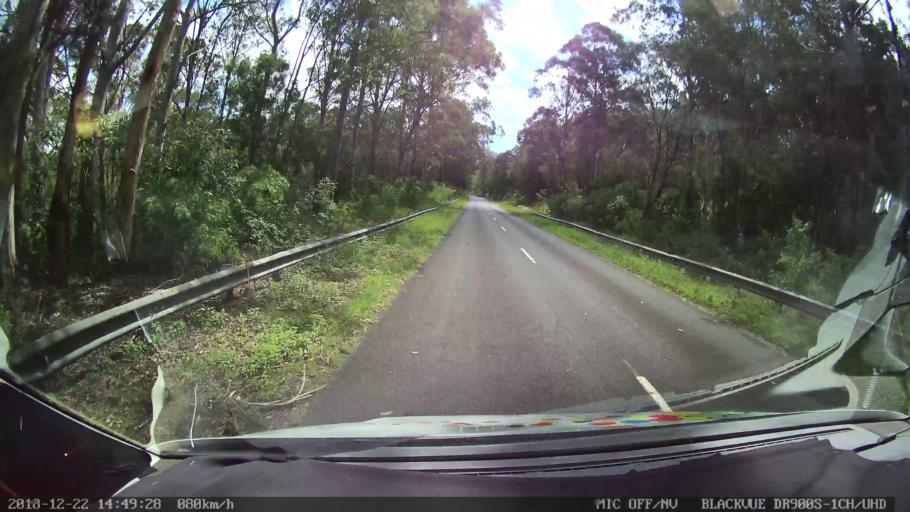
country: AU
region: New South Wales
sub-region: Bellingen
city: Dorrigo
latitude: -30.1888
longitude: 152.5473
